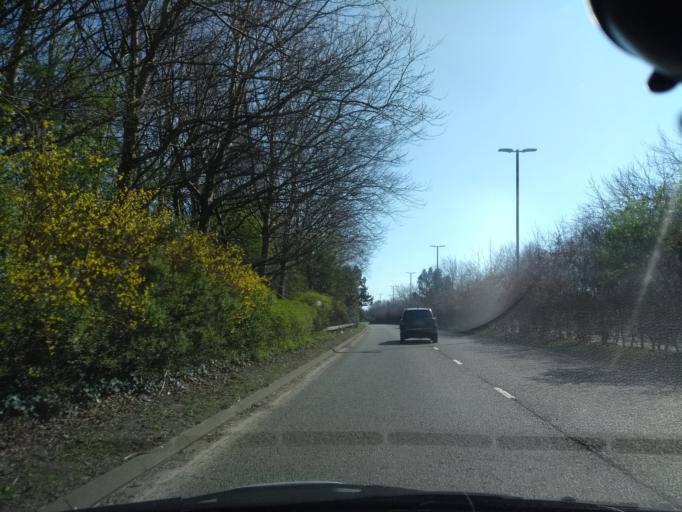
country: GB
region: England
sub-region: Somerset
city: Taunton
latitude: 51.0198
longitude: -3.0901
